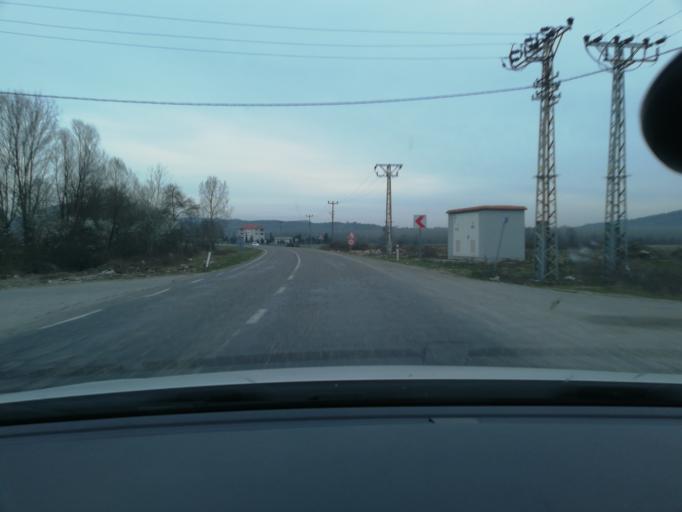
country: TR
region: Zonguldak
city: Saltukova
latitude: 41.5125
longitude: 32.1031
